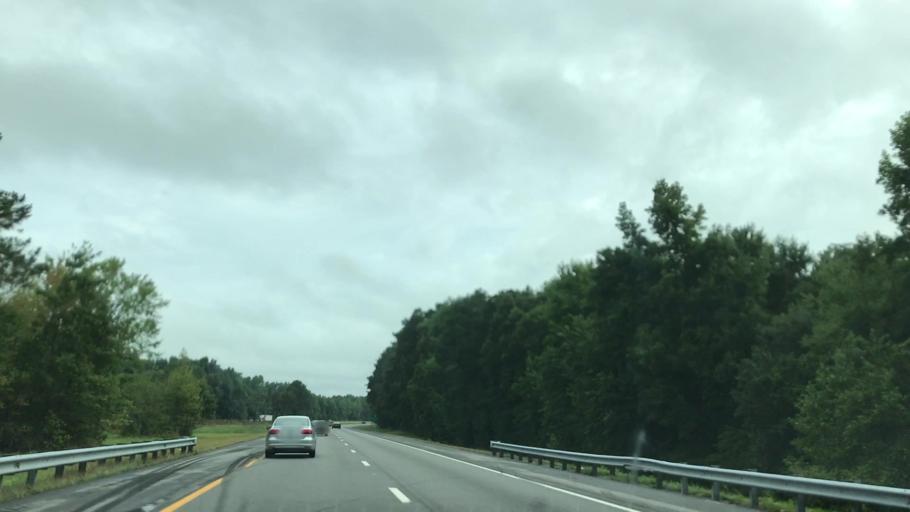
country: US
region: North Carolina
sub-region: Nash County
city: Red Oak
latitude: 36.1081
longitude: -77.8043
